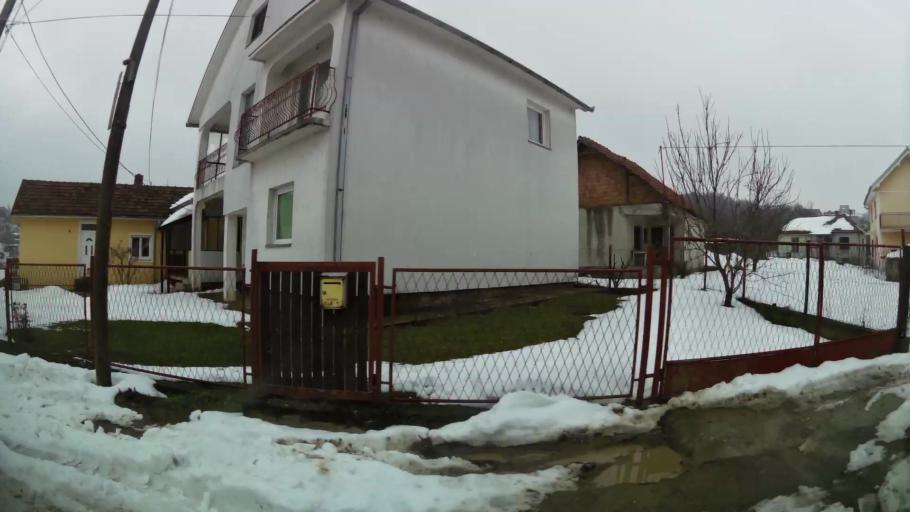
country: RS
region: Central Serbia
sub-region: Belgrade
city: Zvezdara
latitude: 44.7526
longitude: 20.5235
